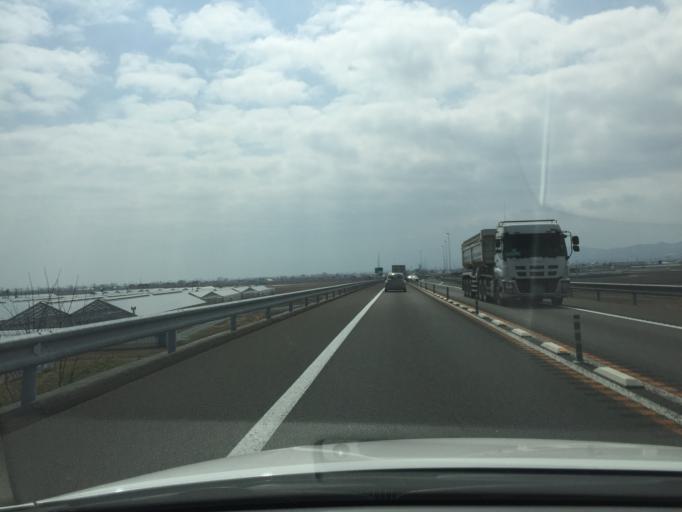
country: JP
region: Miyagi
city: Watari
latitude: 38.0430
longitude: 140.8931
